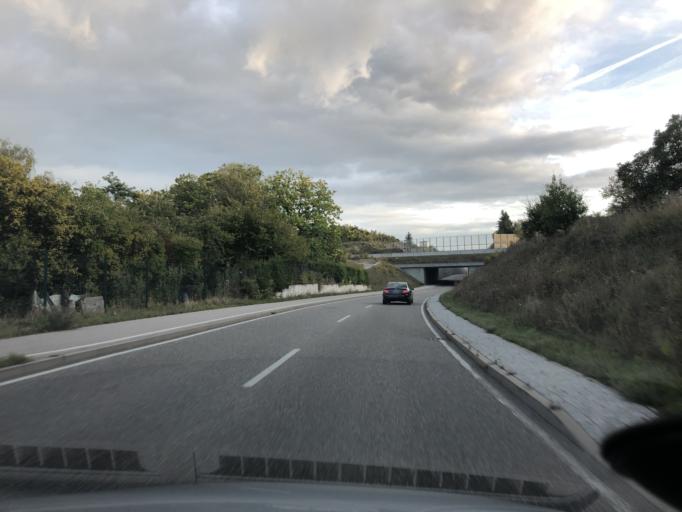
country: DE
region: Baden-Wuerttemberg
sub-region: Karlsruhe Region
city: Wimsheim
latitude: 48.8418
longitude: 8.8305
